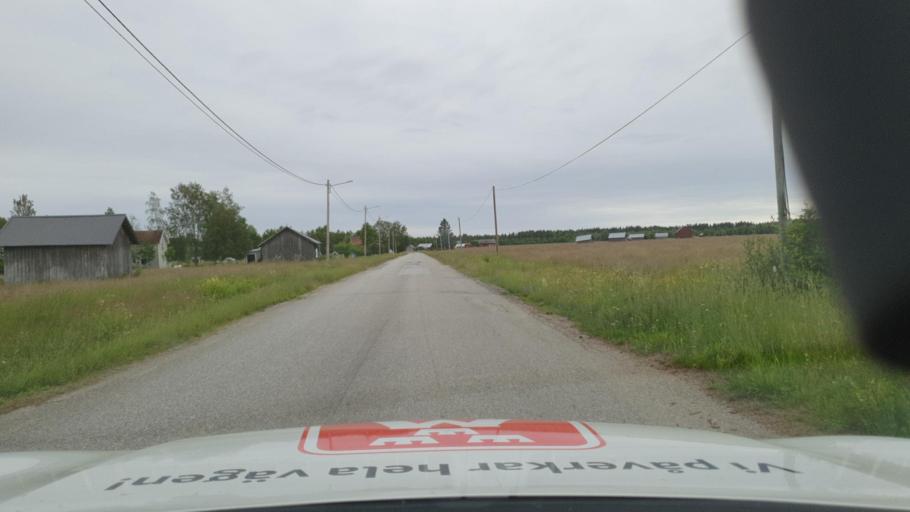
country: SE
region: Vaesterbotten
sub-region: Nordmalings Kommun
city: Nordmaling
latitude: 63.5445
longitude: 19.3928
